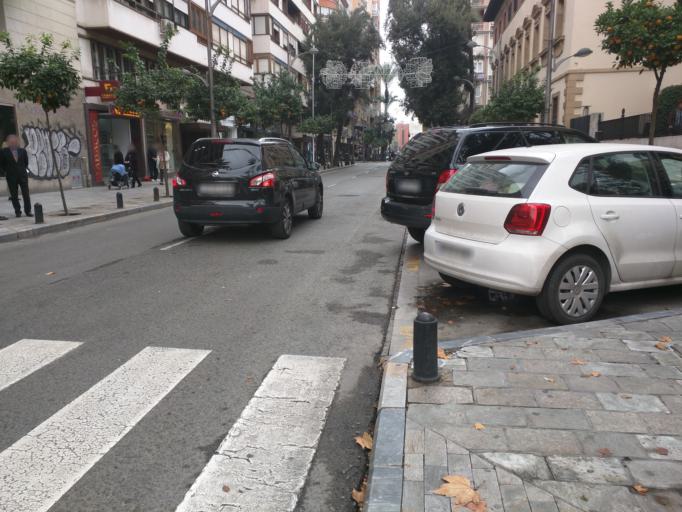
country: ES
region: Murcia
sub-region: Murcia
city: Murcia
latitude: 37.9895
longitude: -1.1302
